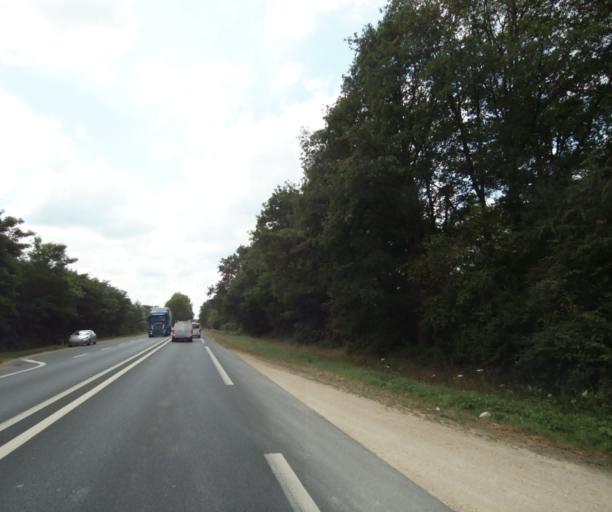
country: FR
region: Centre
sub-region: Departement du Loiret
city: Saint-Cyr-en-Val
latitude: 47.8206
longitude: 1.9247
